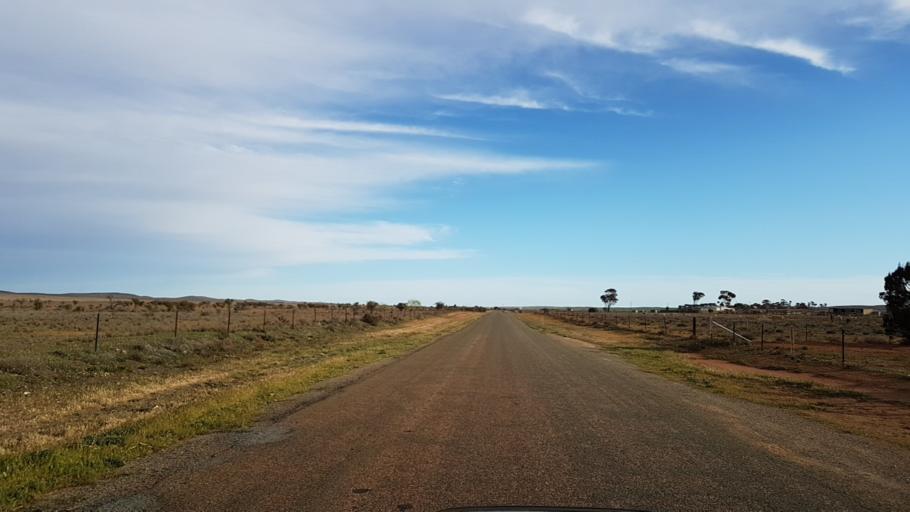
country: AU
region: South Australia
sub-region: Peterborough
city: Peterborough
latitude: -32.9840
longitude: 138.8509
